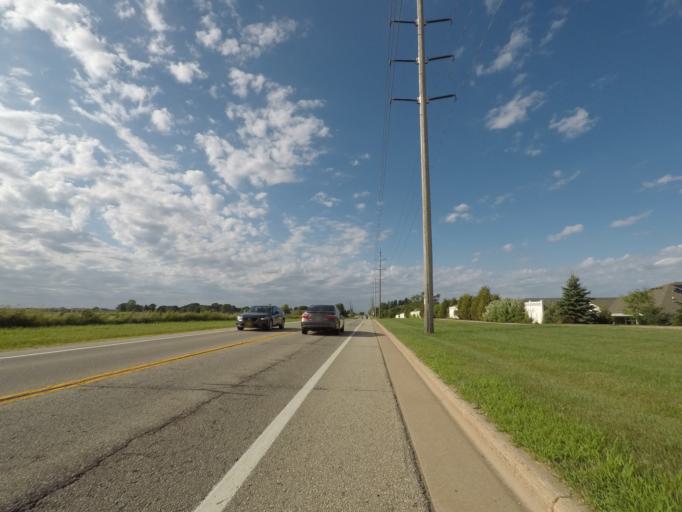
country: US
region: Wisconsin
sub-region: Dane County
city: Middleton
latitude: 43.0689
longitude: -89.5370
